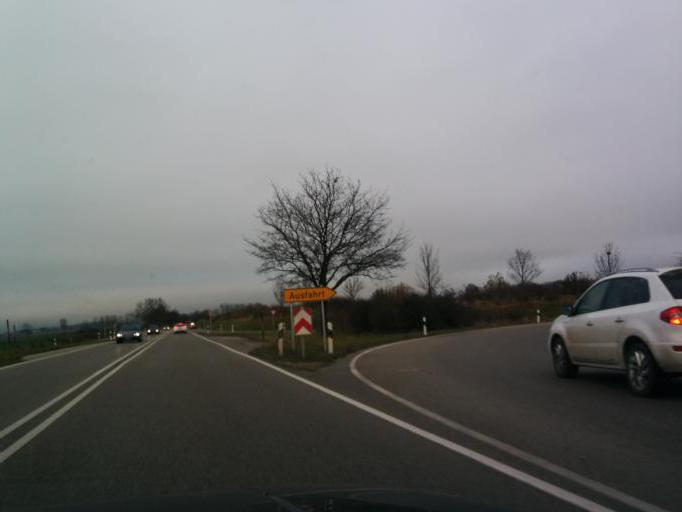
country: DE
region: Bavaria
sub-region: Swabia
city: Rieden
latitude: 47.9223
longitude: 10.6590
